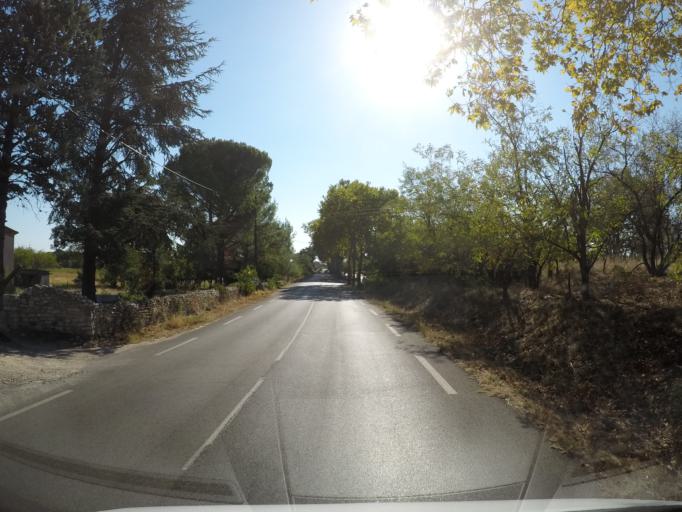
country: FR
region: Languedoc-Roussillon
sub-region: Departement du Gard
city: Boisset-et-Gaujac
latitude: 44.0310
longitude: 4.0122
